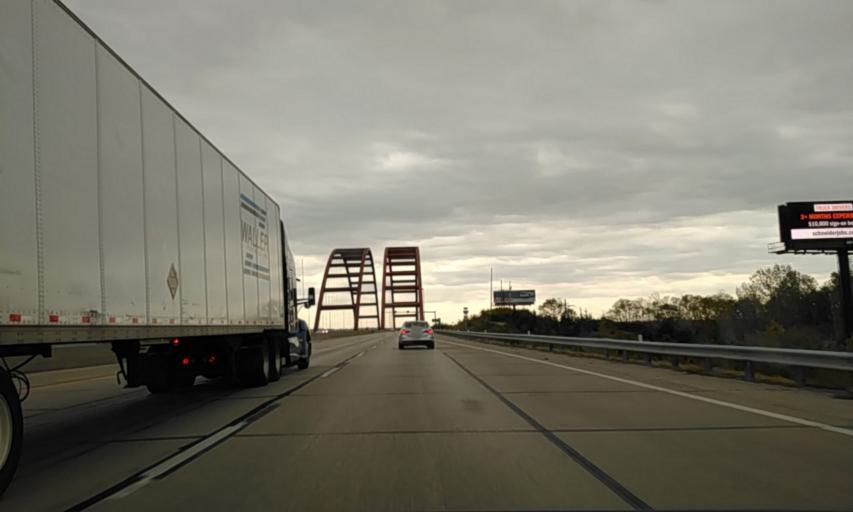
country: US
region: Missouri
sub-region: Saint Louis County
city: Oakville
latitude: 38.4885
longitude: -90.2823
